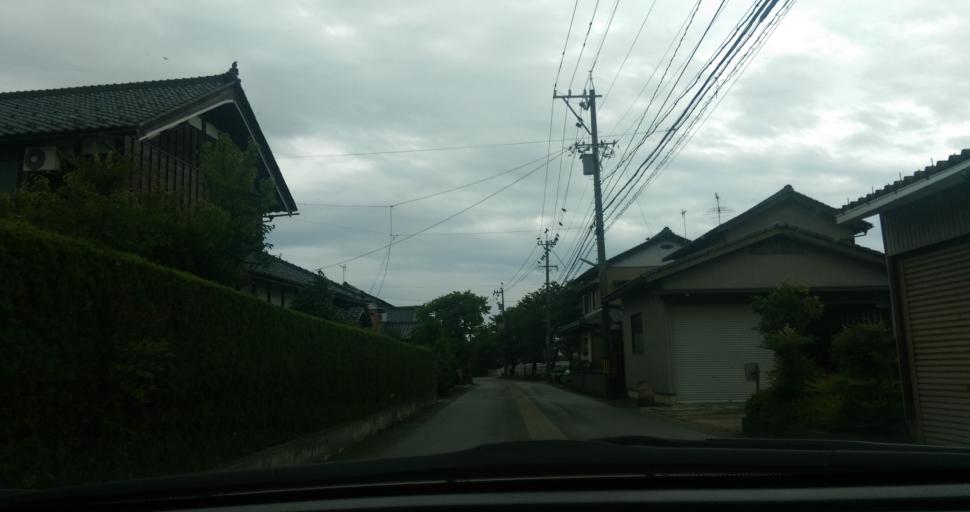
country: JP
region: Fukui
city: Fukui-shi
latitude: 36.0127
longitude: 136.2012
